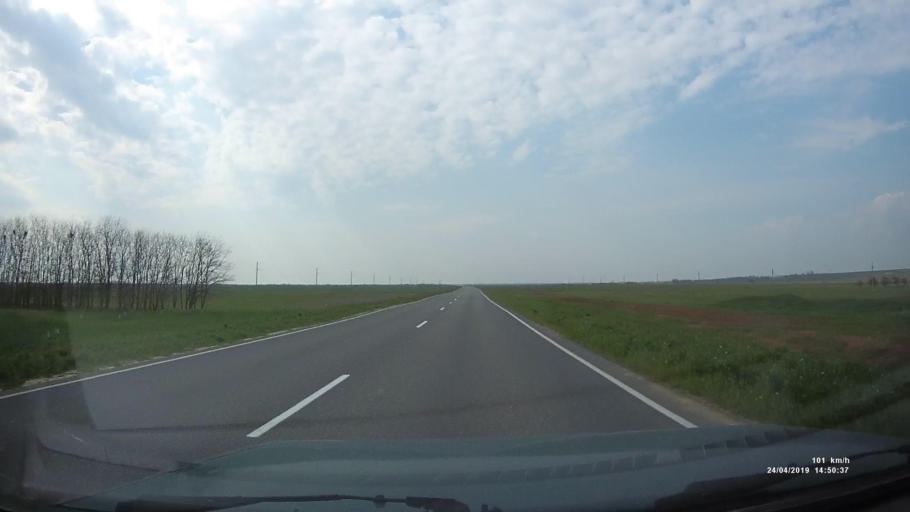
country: RU
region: Rostov
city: Remontnoye
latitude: 46.5186
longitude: 43.7162
